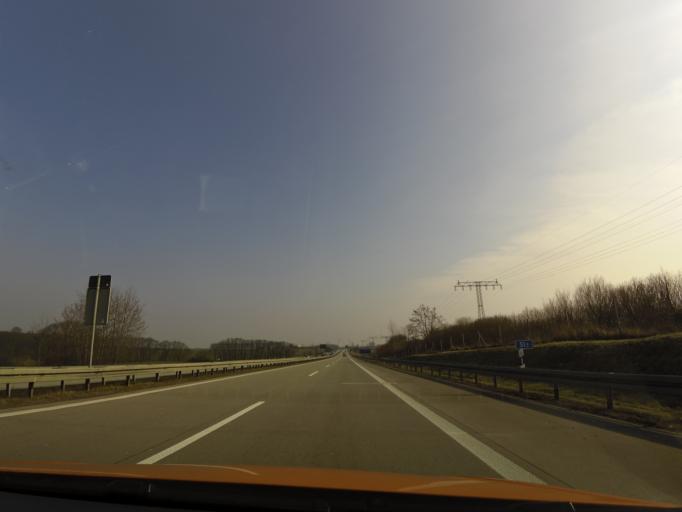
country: DE
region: Brandenburg
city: Frankfurt (Oder)
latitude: 52.3202
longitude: 14.4853
